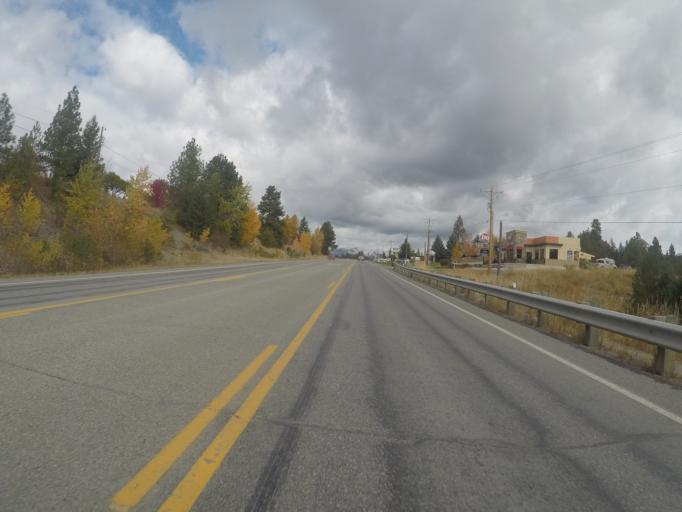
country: US
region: Montana
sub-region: Flathead County
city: Bigfork
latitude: 48.0706
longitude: -114.0801
